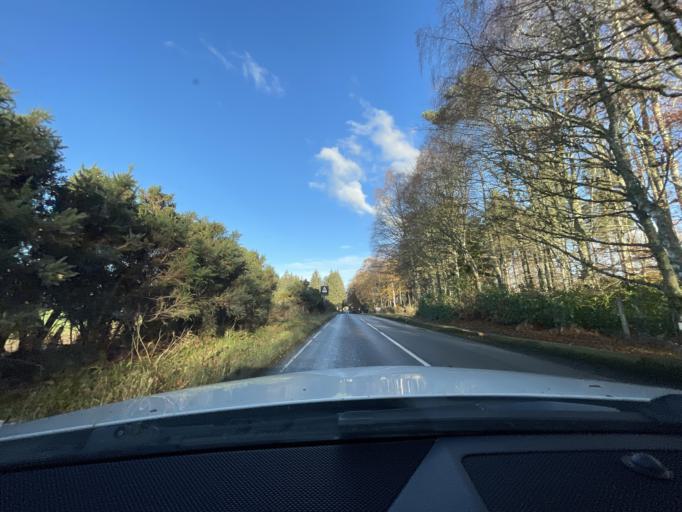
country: GB
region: Scotland
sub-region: Highland
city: Inverness
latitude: 57.3937
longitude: -4.3224
